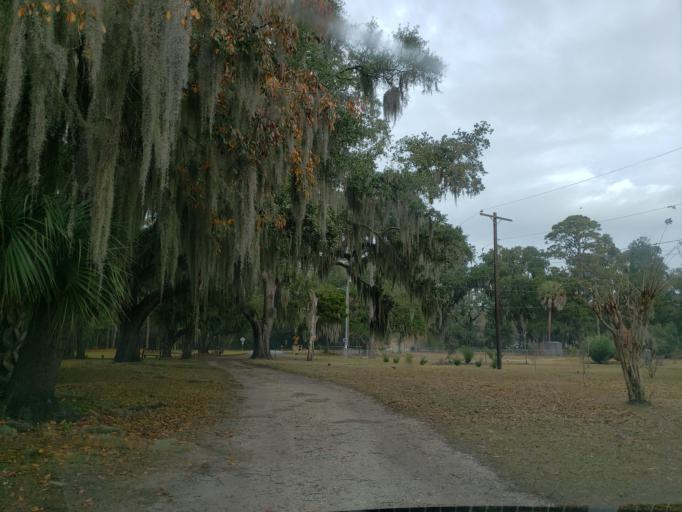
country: US
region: Georgia
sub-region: Chatham County
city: Wilmington Island
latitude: 31.9742
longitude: -80.9976
